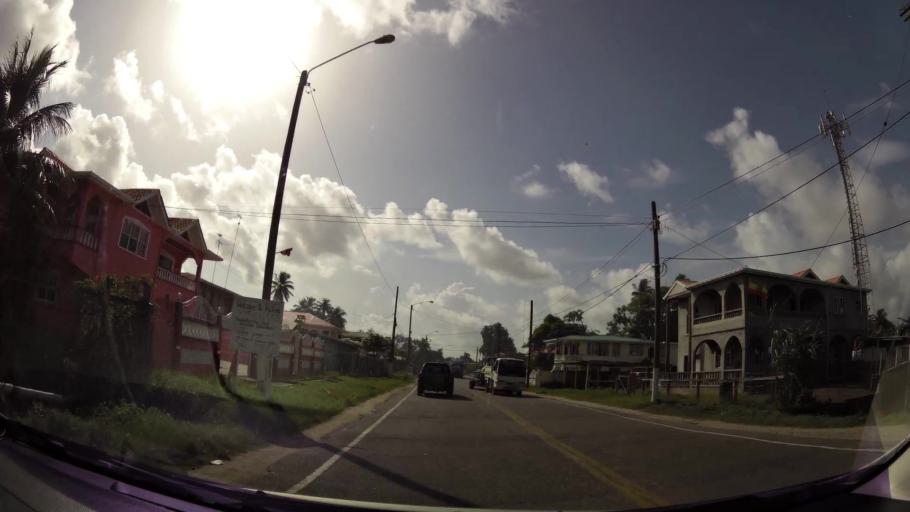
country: GY
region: Demerara-Mahaica
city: Mahaica Village
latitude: 6.7500
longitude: -57.9688
